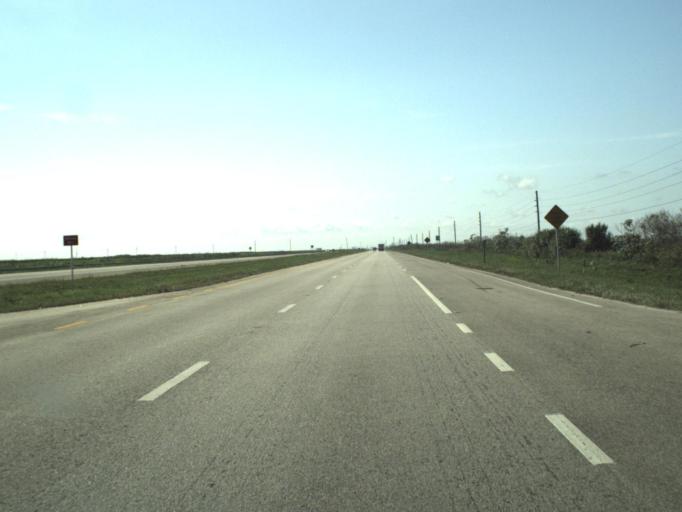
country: US
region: Florida
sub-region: Palm Beach County
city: Belle Glade Camp
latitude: 26.4143
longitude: -80.5994
